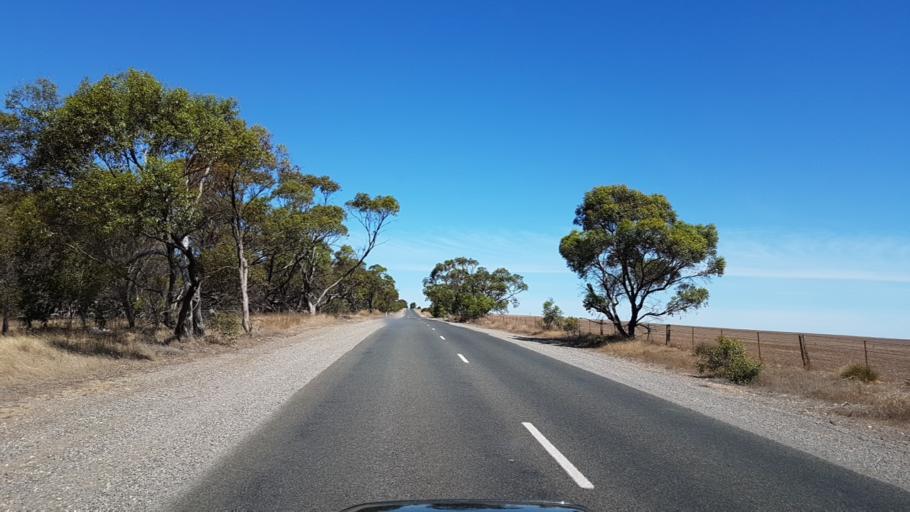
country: AU
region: South Australia
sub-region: Yorke Peninsula
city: Maitland
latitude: -34.3386
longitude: 137.6570
